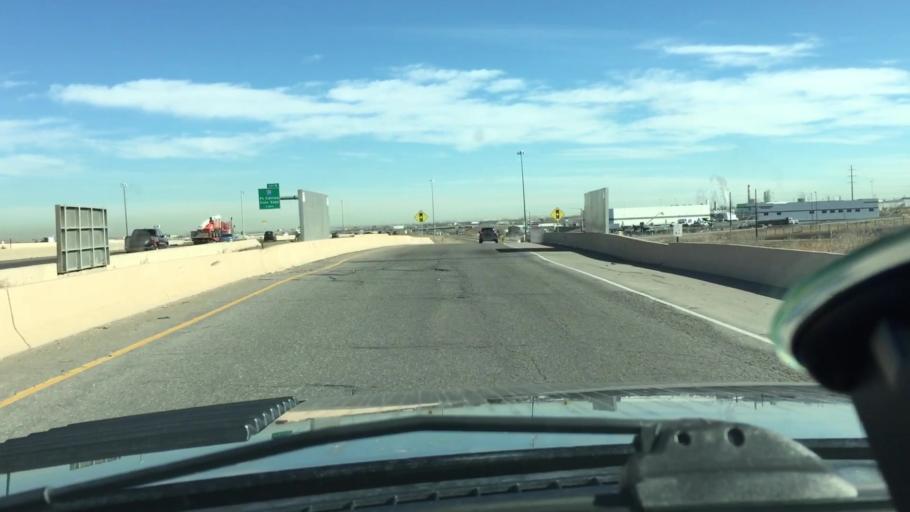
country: US
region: Colorado
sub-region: Adams County
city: Berkley
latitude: 39.8075
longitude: -105.0099
